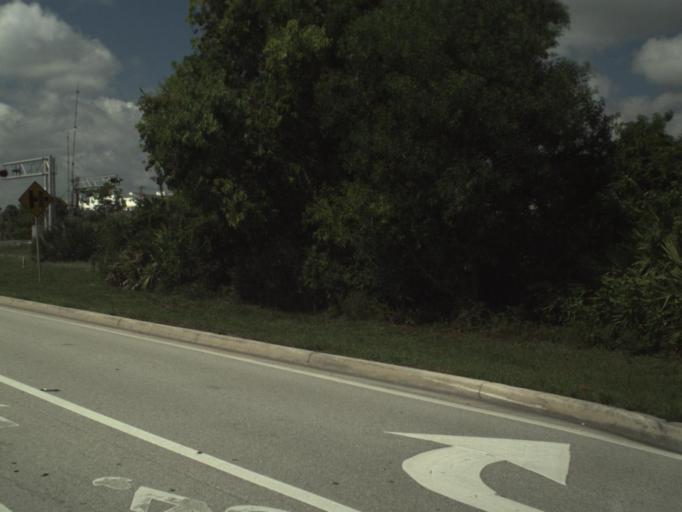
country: US
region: Florida
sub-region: Palm Beach County
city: Jupiter
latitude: 26.9270
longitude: -80.0938
